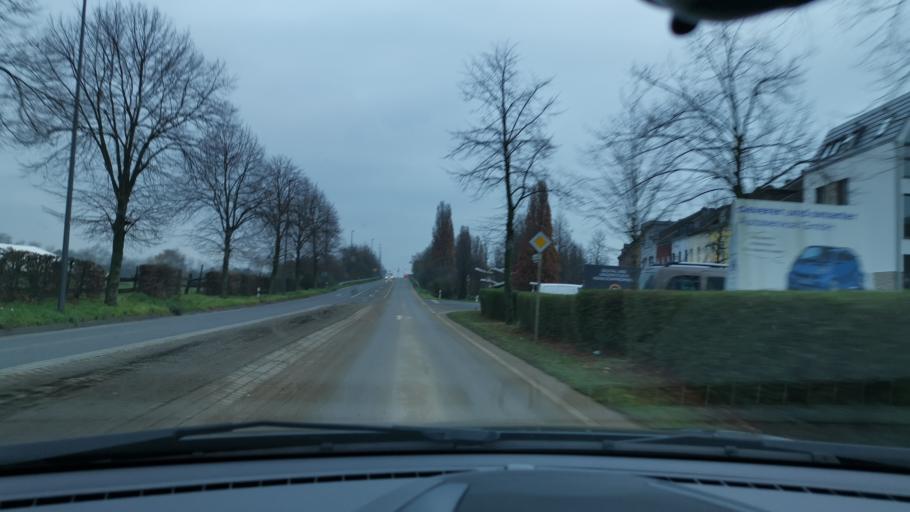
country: DE
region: North Rhine-Westphalia
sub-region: Regierungsbezirk Dusseldorf
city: Grevenbroich
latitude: 51.0861
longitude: 6.6043
